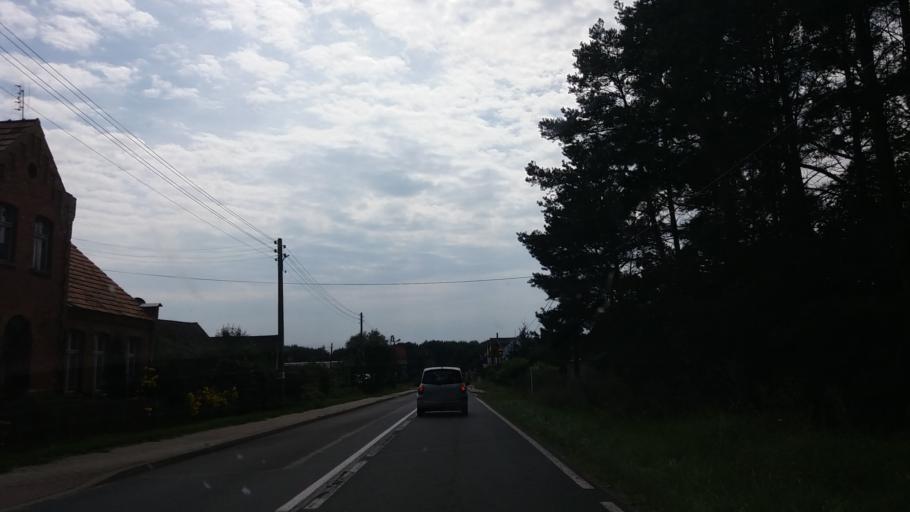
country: PL
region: Lubusz
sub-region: Powiat strzelecko-drezdenecki
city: Zwierzyn
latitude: 52.7273
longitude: 15.6184
